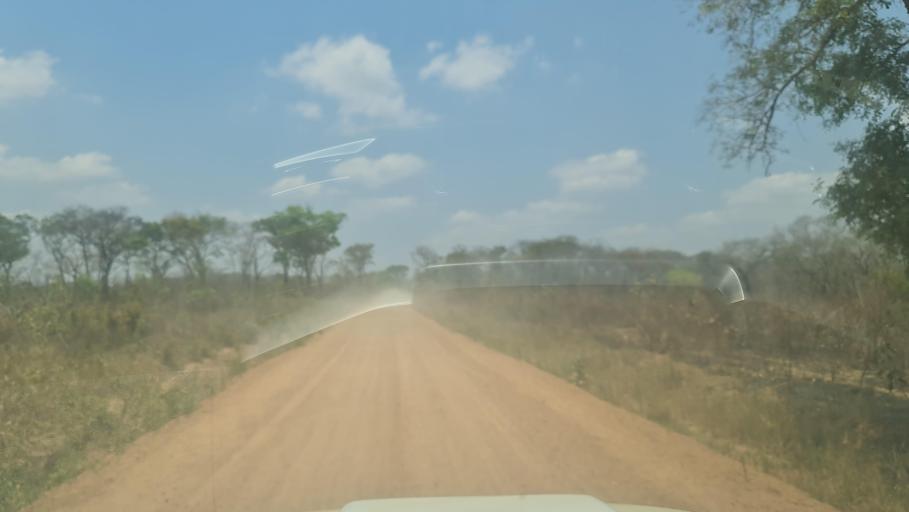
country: MW
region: Southern Region
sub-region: Nsanje District
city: Nsanje
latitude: -17.5565
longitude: 35.8965
